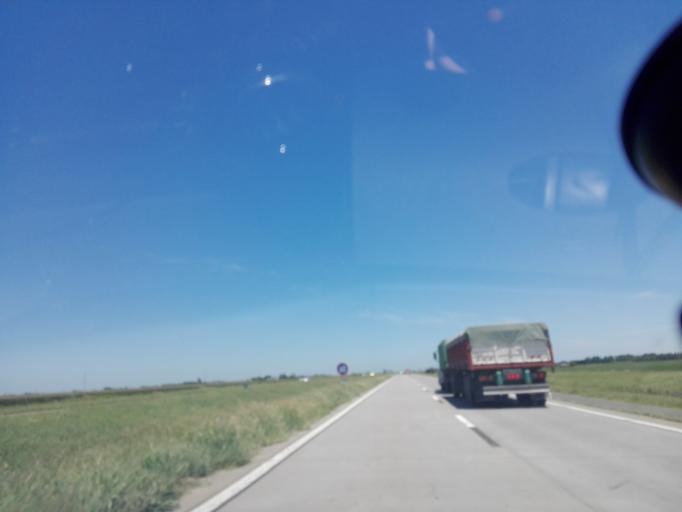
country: AR
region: Santa Fe
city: Armstrong
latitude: -32.8161
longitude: -61.5675
